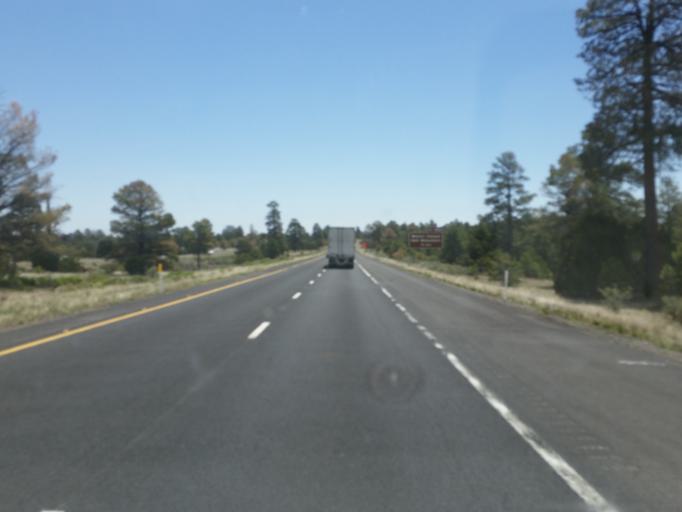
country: US
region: Arizona
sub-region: Coconino County
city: Flagstaff
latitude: 35.2110
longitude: -111.5284
